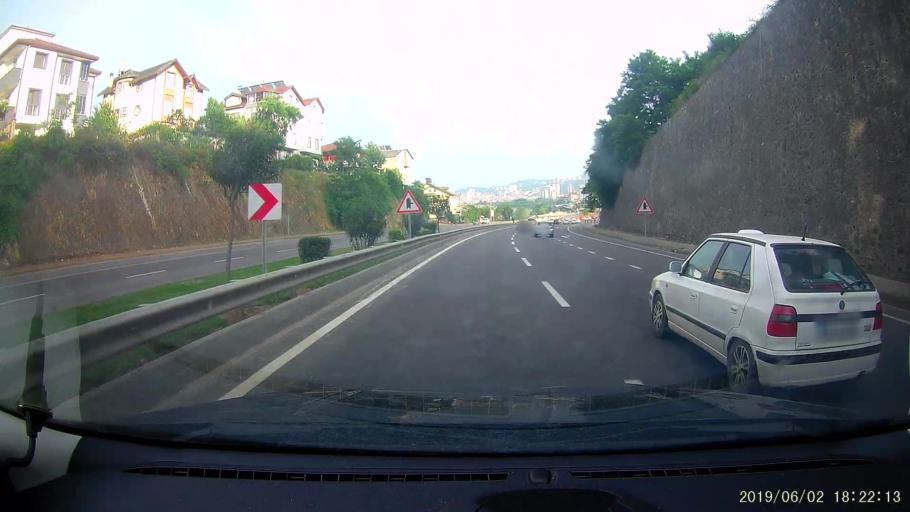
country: TR
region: Ordu
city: Fatsa
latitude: 41.0596
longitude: 37.4762
